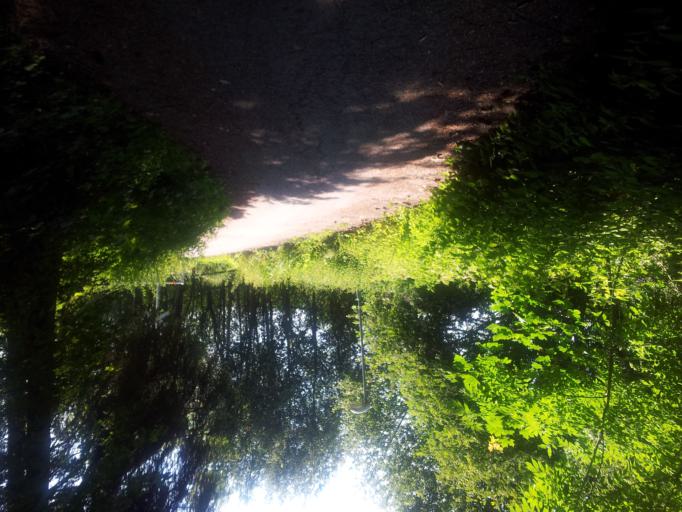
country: SE
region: Uppsala
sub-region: Uppsala Kommun
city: Saevja
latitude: 59.8627
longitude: 17.6968
